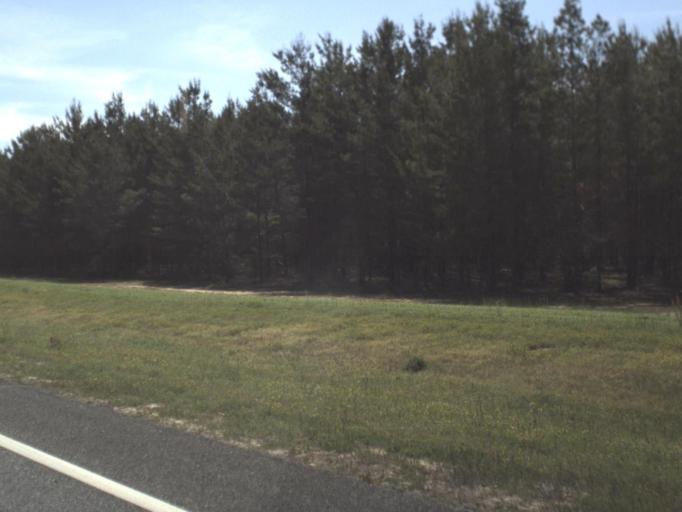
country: US
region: Florida
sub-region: Bay County
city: Lynn Haven
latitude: 30.4352
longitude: -85.6882
